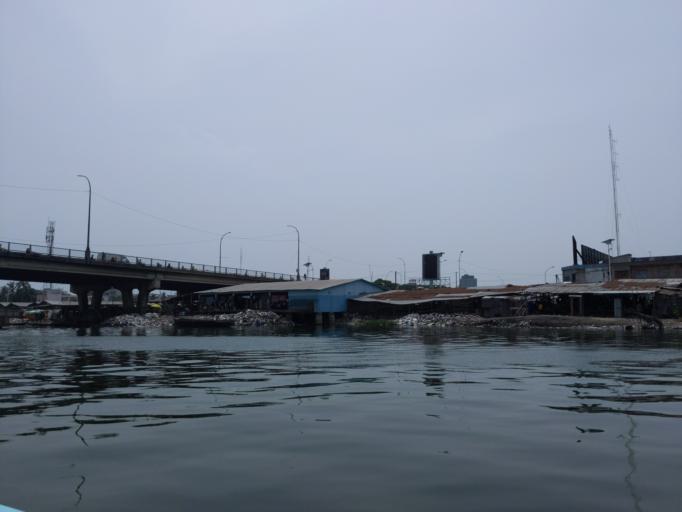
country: BJ
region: Littoral
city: Cotonou
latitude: 6.3717
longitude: 2.4364
